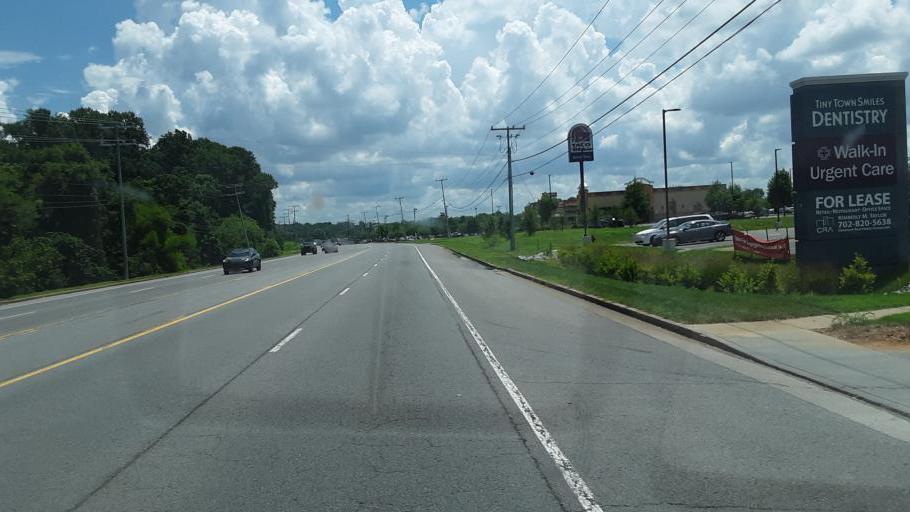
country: US
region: Kentucky
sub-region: Christian County
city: Oak Grove
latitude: 36.6280
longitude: -87.3746
